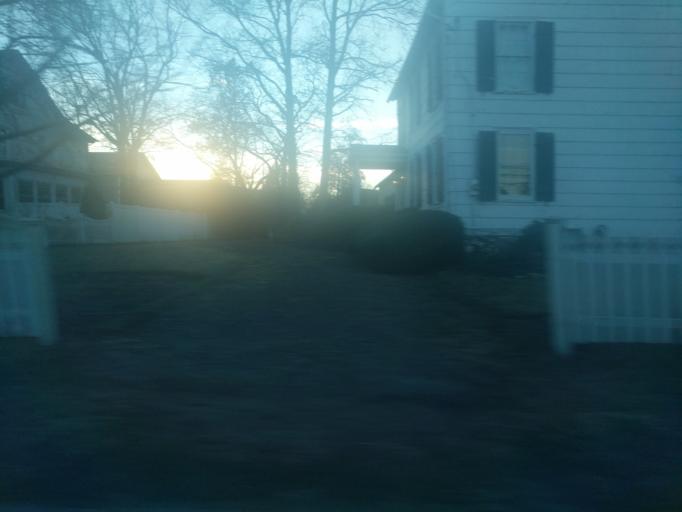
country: US
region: New York
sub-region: Nassau County
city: Wantagh
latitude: 40.6843
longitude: -73.5101
